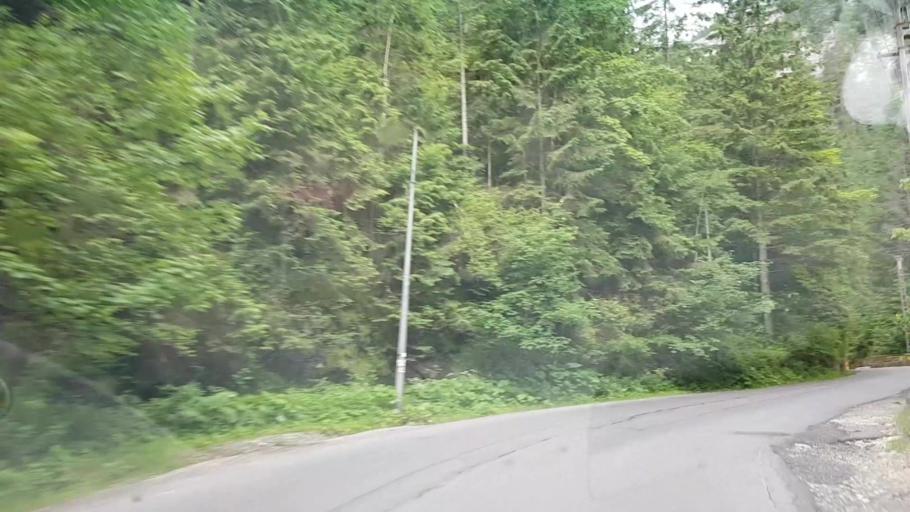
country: RO
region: Neamt
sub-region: Comuna Bicaz Chei
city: Bicaz Chei
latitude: 46.8050
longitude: 25.8083
